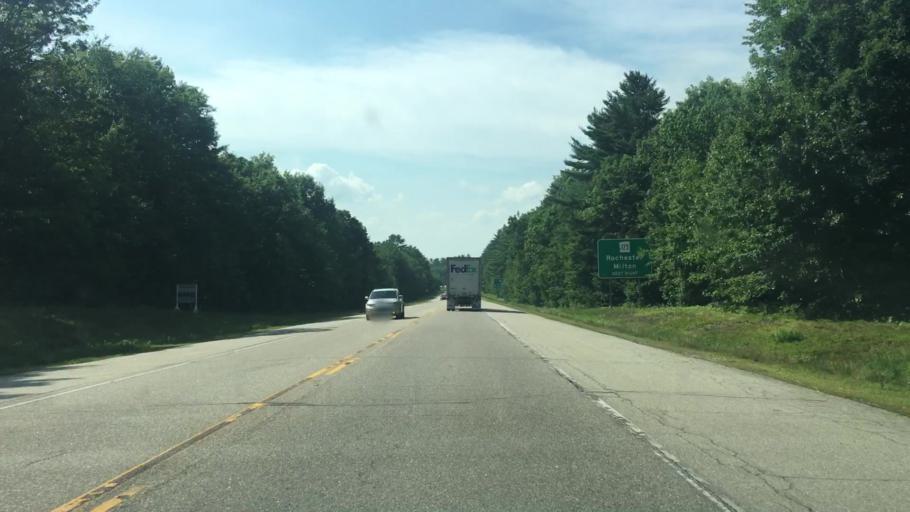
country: US
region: New Hampshire
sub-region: Strafford County
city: Rochester
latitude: 43.3259
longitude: -70.9633
